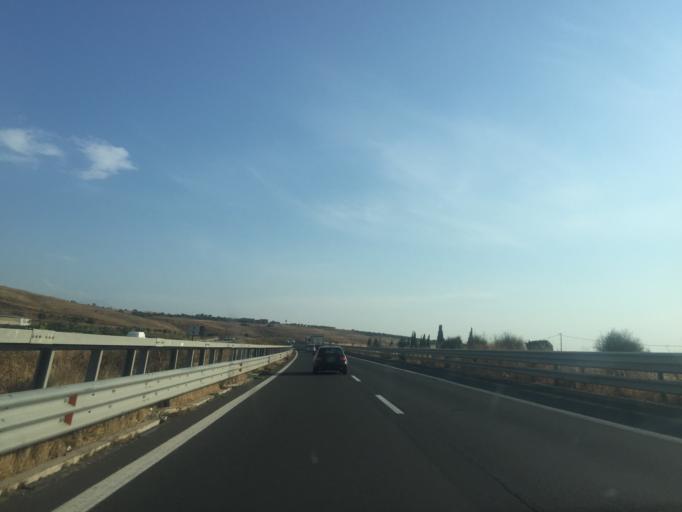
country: IT
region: Sicily
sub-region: Provincia di Siracusa
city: Carlentini
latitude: 37.3534
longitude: 15.0466
